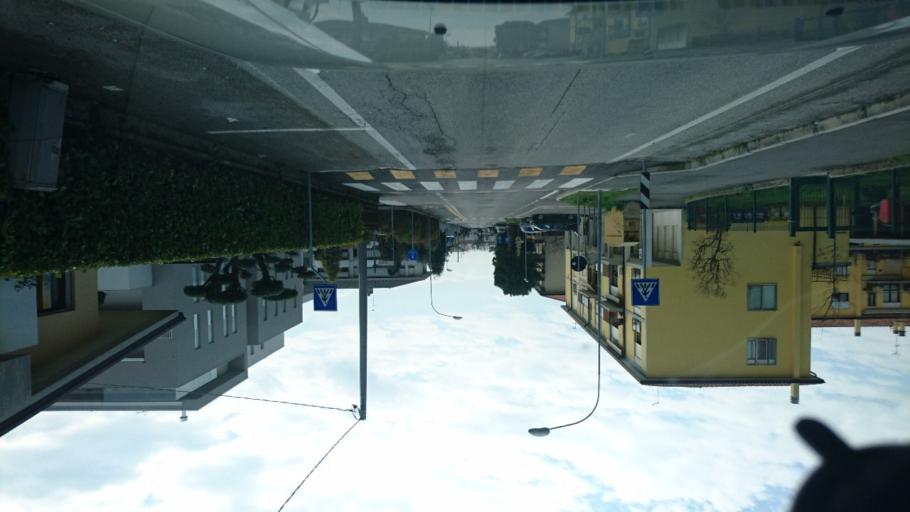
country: IT
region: Veneto
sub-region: Provincia di Padova
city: Noventa
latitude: 45.4097
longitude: 11.9450
